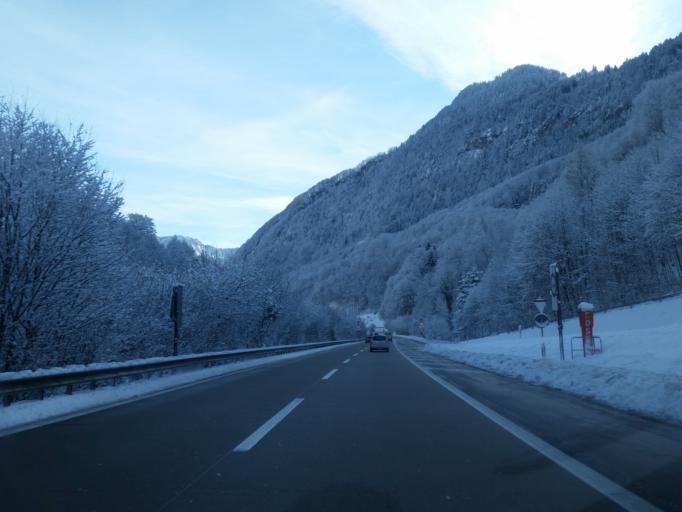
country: CH
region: Saint Gallen
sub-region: Wahlkreis Sarganserland
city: Quarten
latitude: 47.1124
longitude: 9.2683
